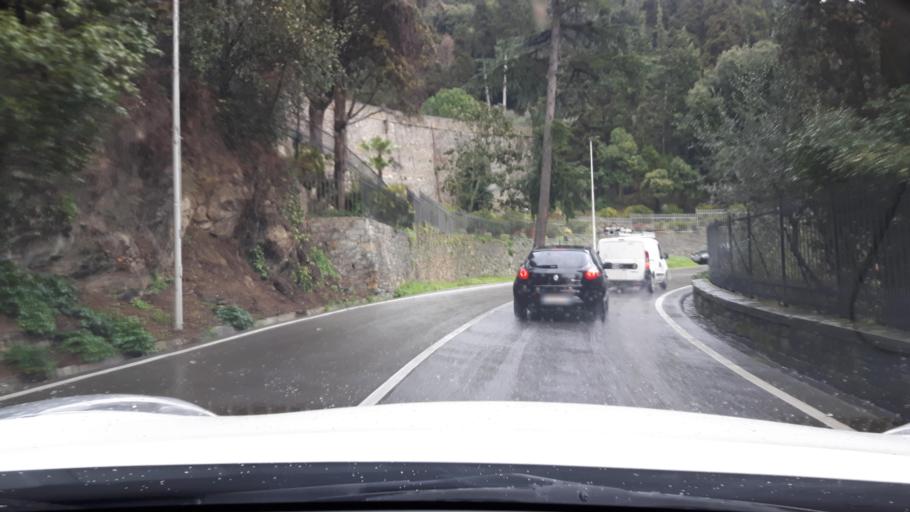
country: IT
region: Tuscany
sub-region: Province of Florence
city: Fiesole
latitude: 43.8016
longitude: 11.2968
